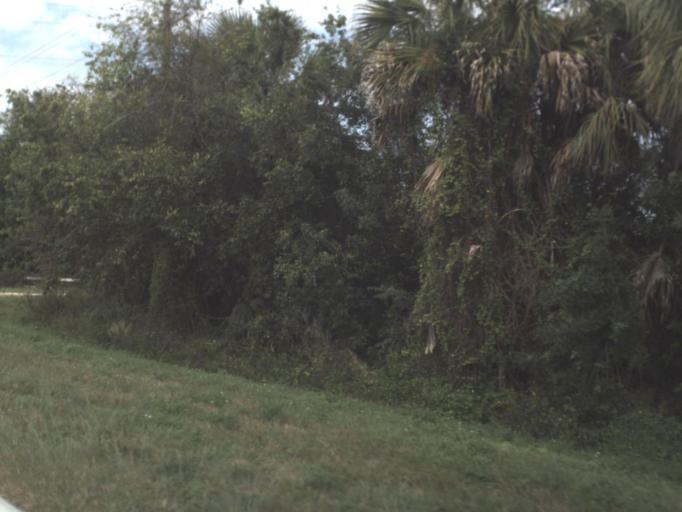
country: US
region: Florida
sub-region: Glades County
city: Moore Haven
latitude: 26.7684
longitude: -81.2040
